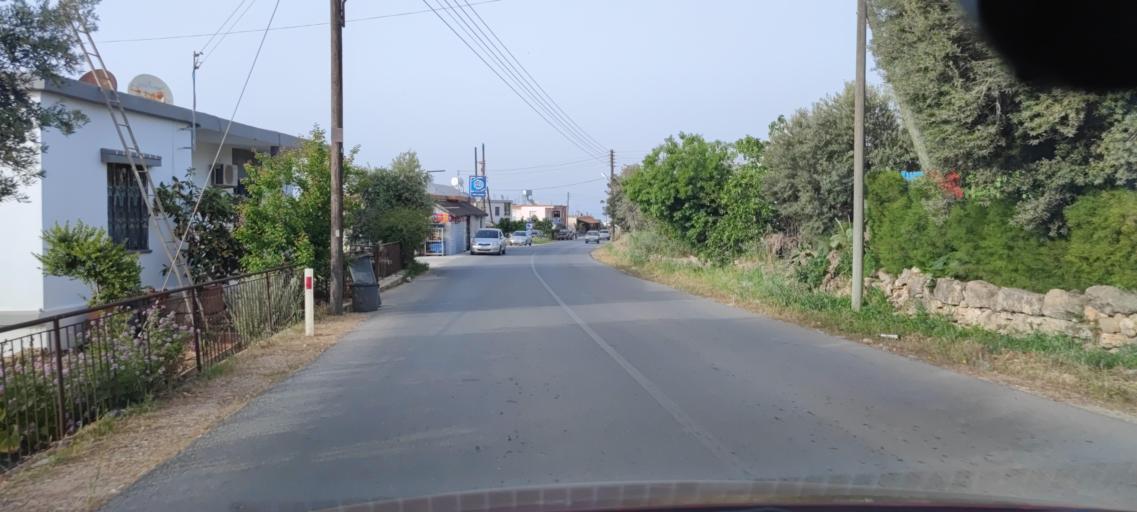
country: CY
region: Ammochostos
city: Leonarisso
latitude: 35.5402
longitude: 34.1941
